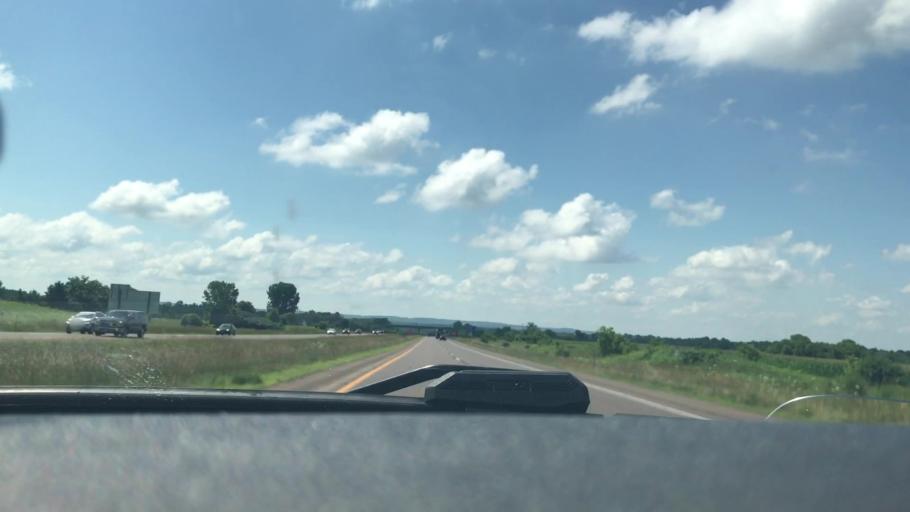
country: US
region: Wisconsin
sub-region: Chippewa County
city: Chippewa Falls
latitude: 44.9483
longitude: -91.4267
